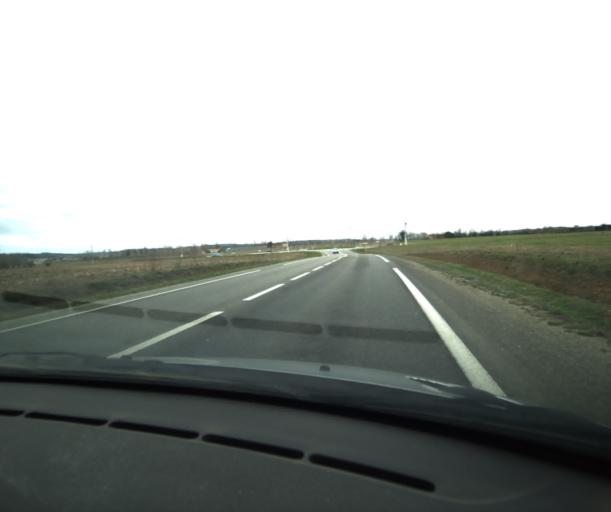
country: FR
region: Midi-Pyrenees
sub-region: Departement du Tarn-et-Garonne
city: Moissac
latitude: 44.0831
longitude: 1.1165
